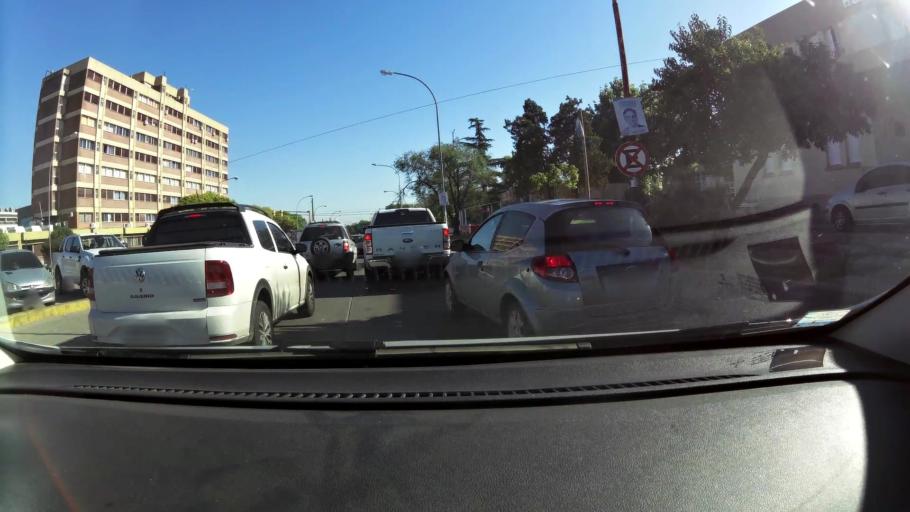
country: AR
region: Cordoba
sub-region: Departamento de Capital
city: Cordoba
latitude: -31.4288
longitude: -64.1697
